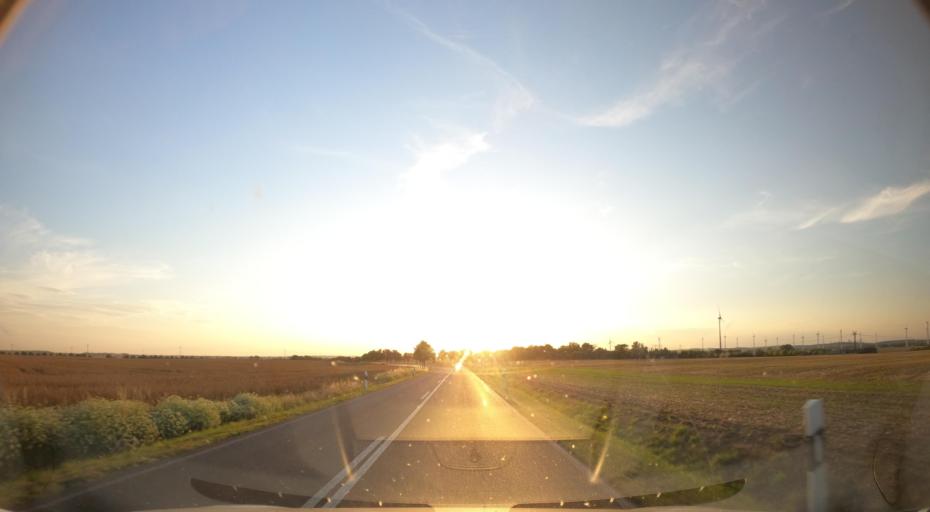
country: DE
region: Mecklenburg-Vorpommern
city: Strasburg
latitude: 53.4896
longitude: 13.8350
